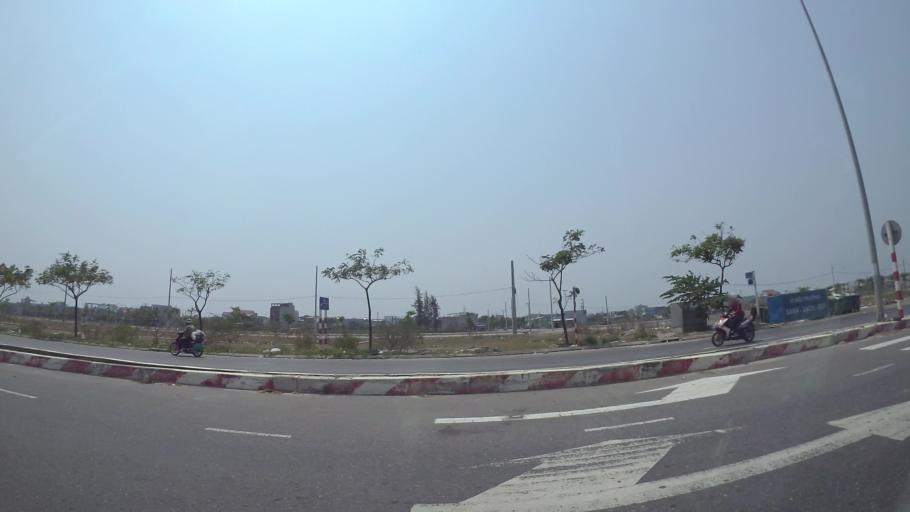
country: VN
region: Da Nang
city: Ngu Hanh Son
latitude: 15.9907
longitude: 108.2378
